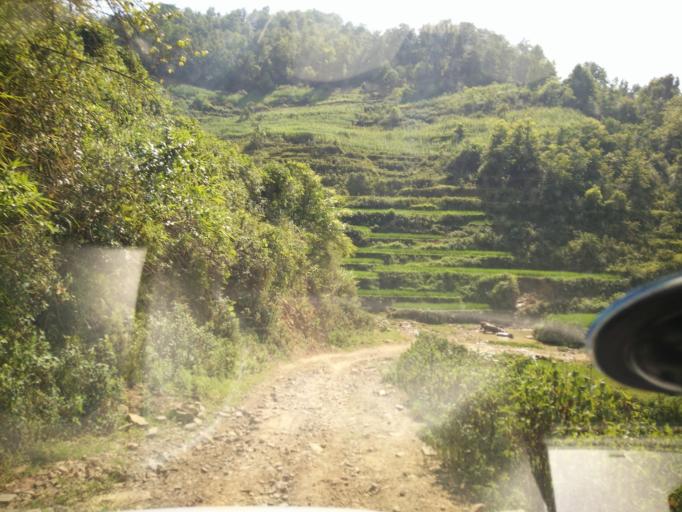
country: CN
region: Guangxi Zhuangzu Zizhiqu
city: Xinzhou
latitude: 25.1877
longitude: 105.6943
